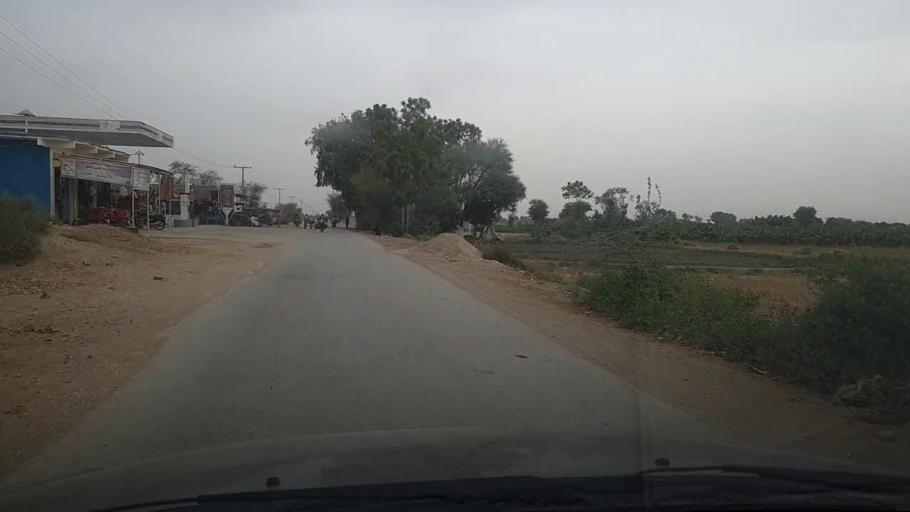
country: PK
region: Sindh
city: Daulatpur
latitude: 26.3148
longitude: 68.1013
